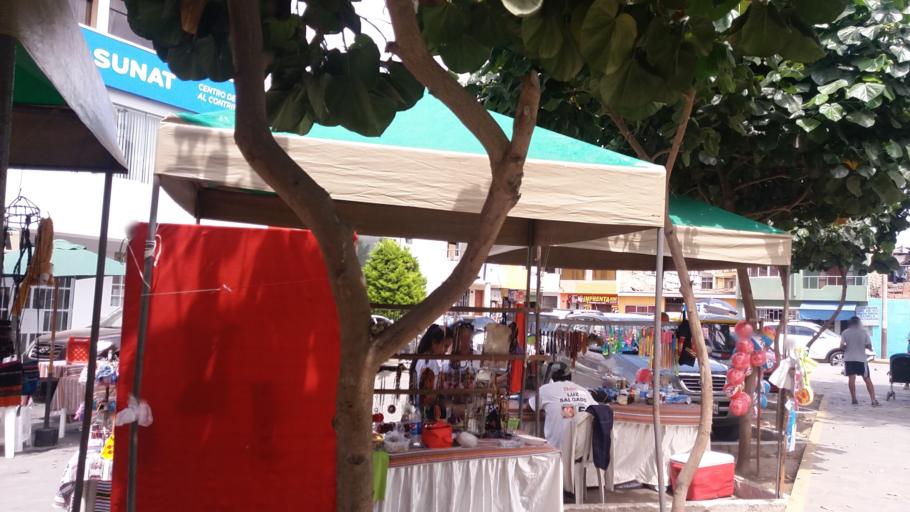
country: PE
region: Lima
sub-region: Lima
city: Punta Hermosa
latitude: -12.2732
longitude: -76.8688
